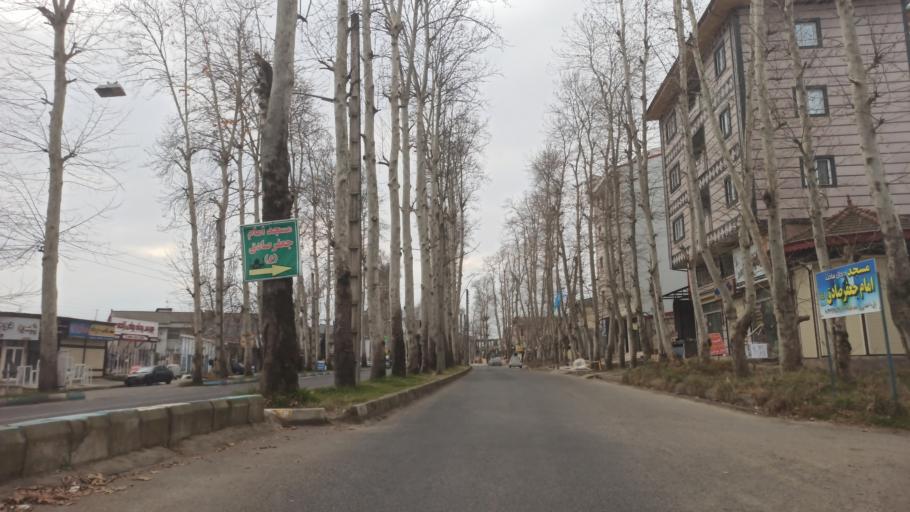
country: IR
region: Gilan
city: Fuman
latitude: 37.2354
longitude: 49.3246
